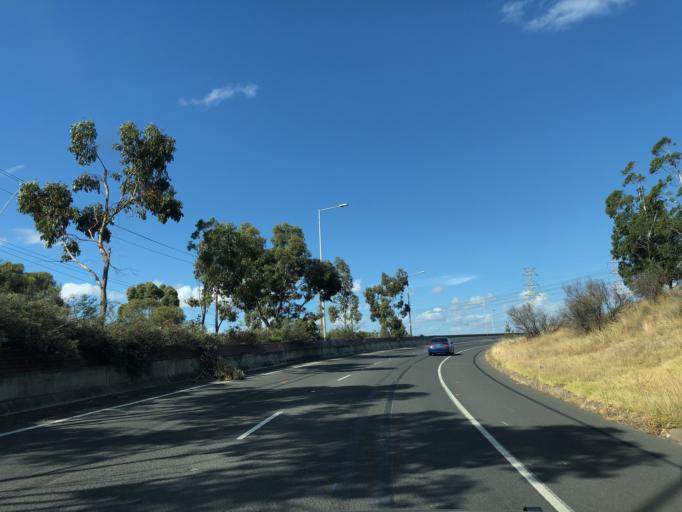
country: AU
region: Victoria
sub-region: Brimbank
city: Keilor Park
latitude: -37.7262
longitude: 144.8598
